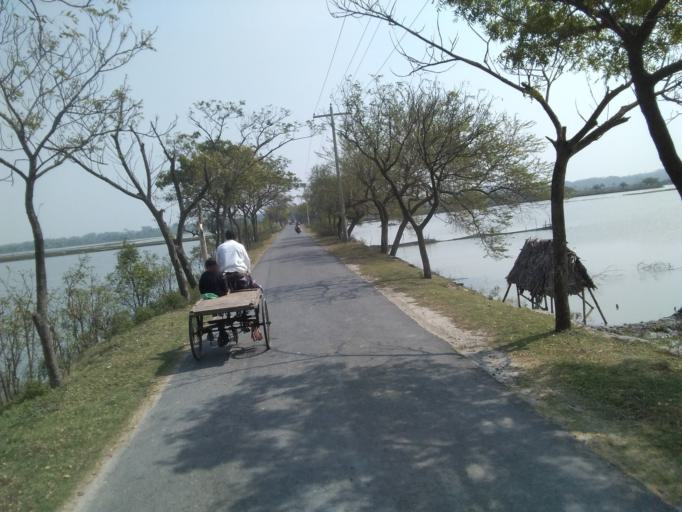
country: IN
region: West Bengal
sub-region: North 24 Parganas
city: Taki
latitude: 22.5937
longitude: 88.9841
